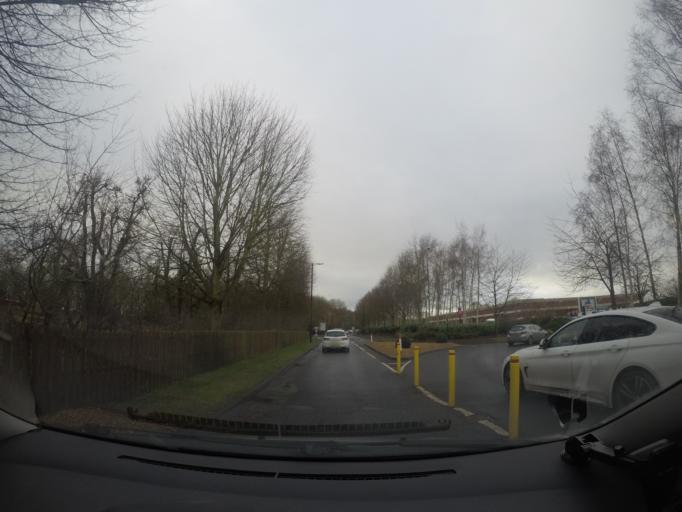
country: GB
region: England
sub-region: City of York
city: Fulford
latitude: 53.9213
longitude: -1.0737
